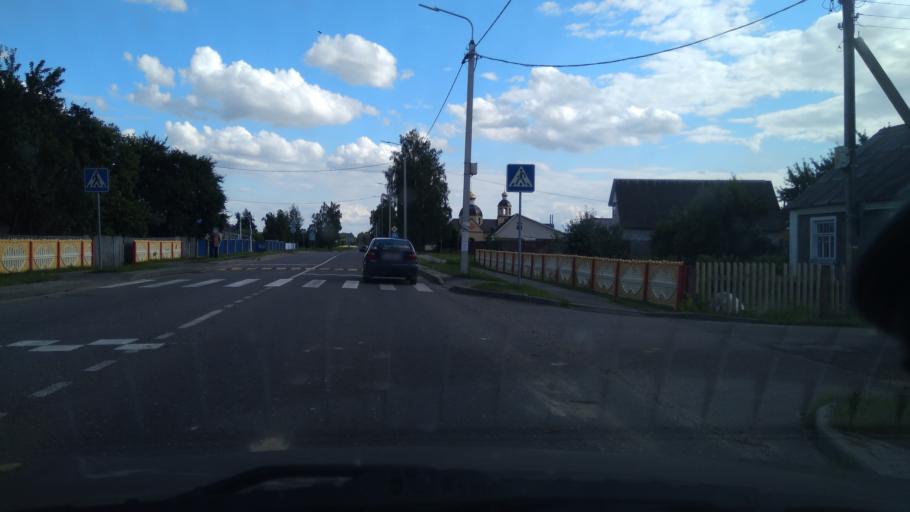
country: BY
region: Grodnenskaya
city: Masty
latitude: 53.3949
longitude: 24.5399
